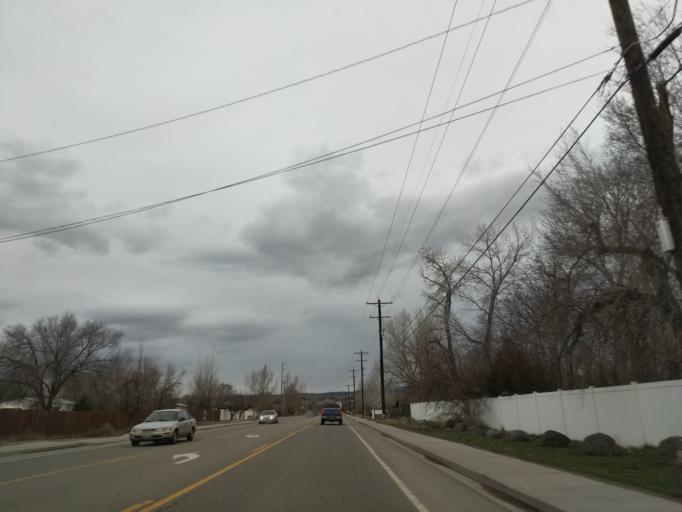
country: US
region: Colorado
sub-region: Mesa County
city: Fruitvale
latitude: 39.0583
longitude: -108.5152
